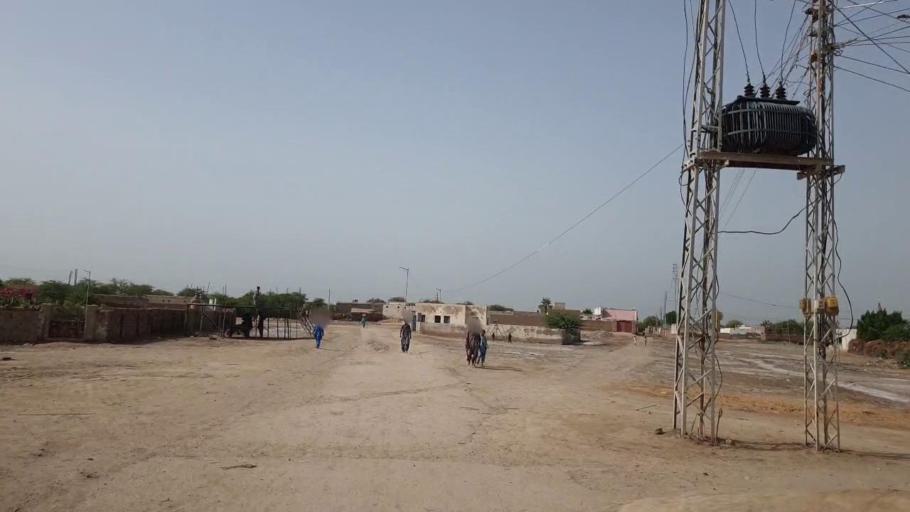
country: PK
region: Sindh
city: Jam Sahib
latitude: 26.2927
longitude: 68.6311
